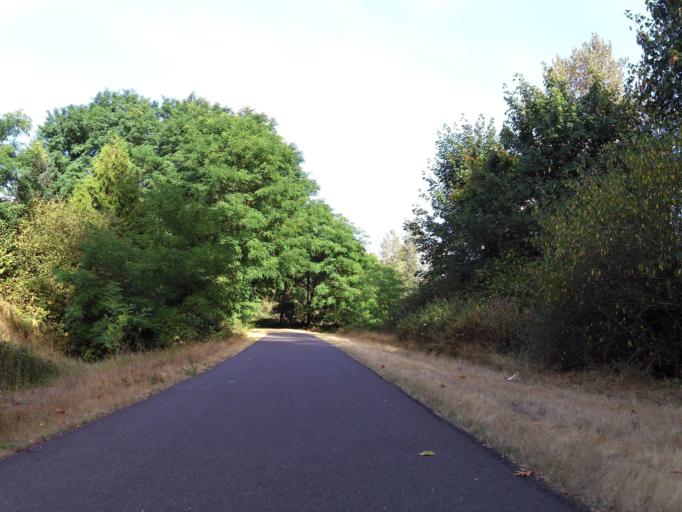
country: US
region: Washington
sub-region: Thurston County
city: Lacey
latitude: 47.0394
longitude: -122.8550
